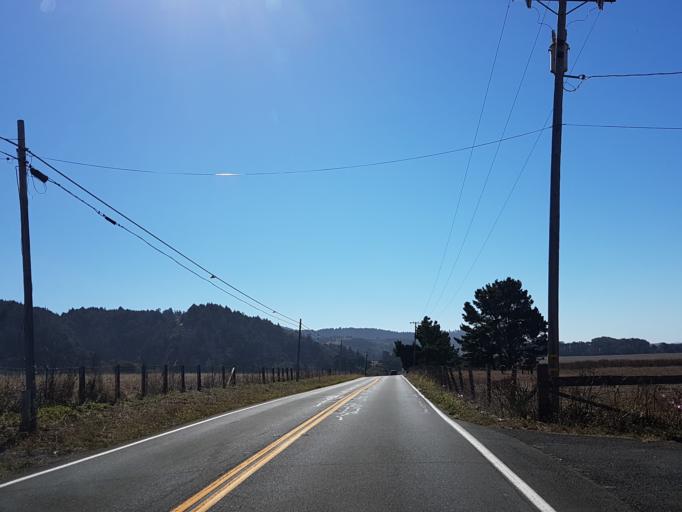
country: US
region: California
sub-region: Mendocino County
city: Boonville
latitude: 39.0665
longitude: -123.6902
